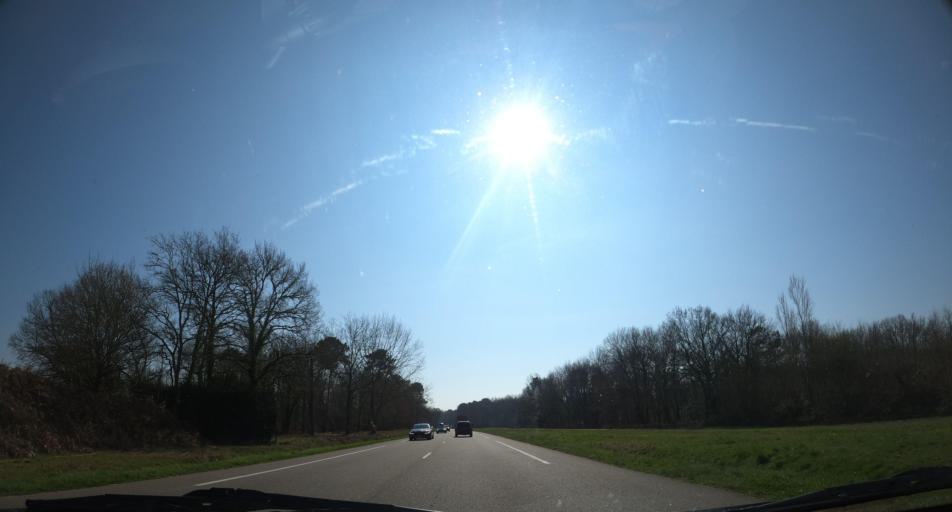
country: FR
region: Aquitaine
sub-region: Departement des Landes
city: Saint-Pierre-du-Mont
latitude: 43.8746
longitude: -0.5209
